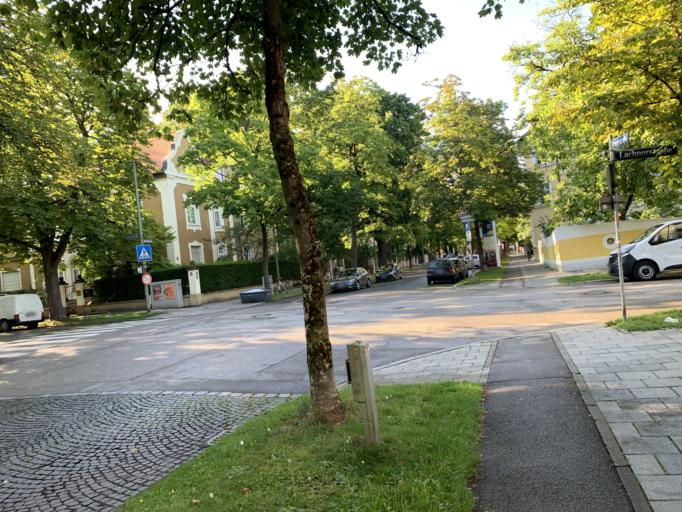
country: DE
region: Bavaria
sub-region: Upper Bavaria
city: Munich
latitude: 48.1554
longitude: 11.5271
